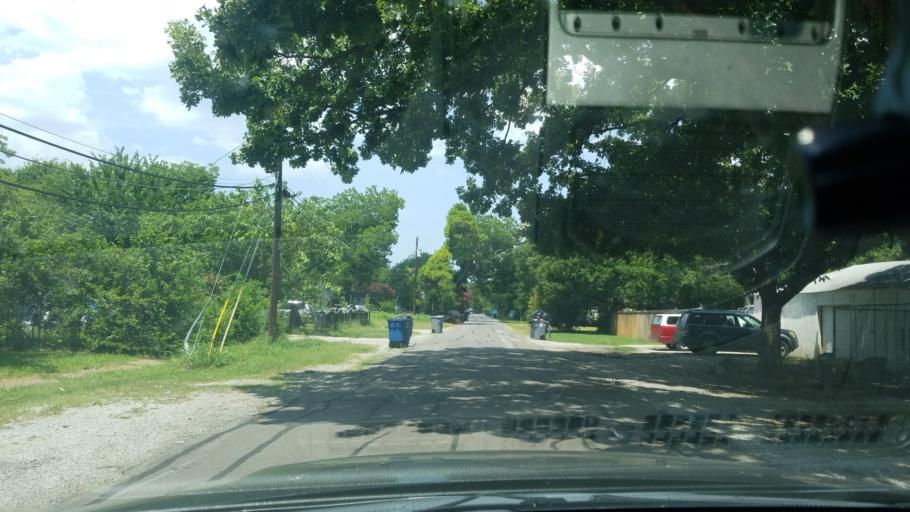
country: US
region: Texas
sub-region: Dallas County
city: Balch Springs
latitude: 32.7302
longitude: -96.6903
